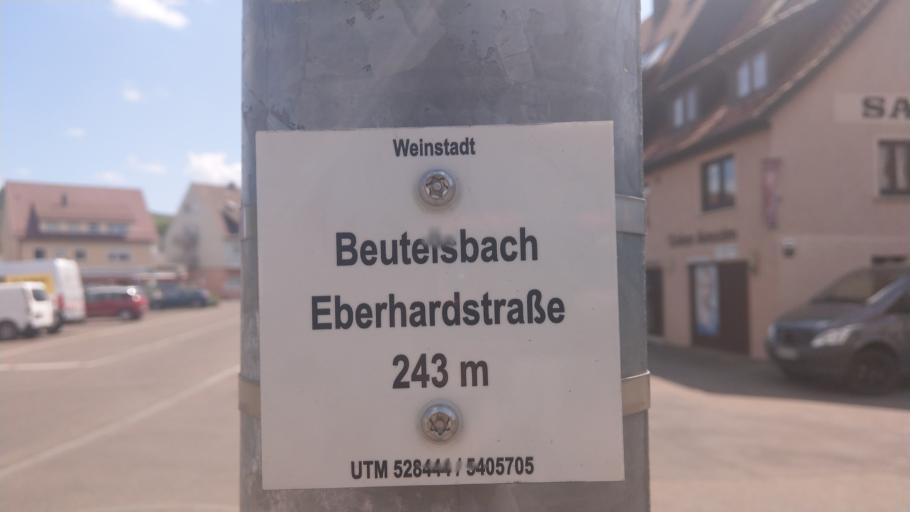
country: DE
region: Baden-Wuerttemberg
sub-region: Regierungsbezirk Stuttgart
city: Weinstadt-Endersbach
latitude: 48.8037
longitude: 9.3874
